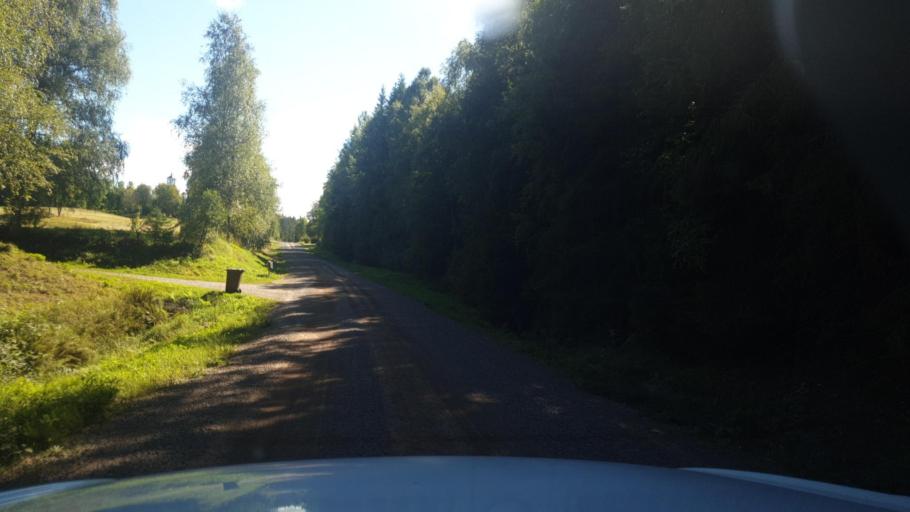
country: SE
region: Vaermland
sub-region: Eda Kommun
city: Charlottenberg
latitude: 60.0609
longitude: 12.5500
